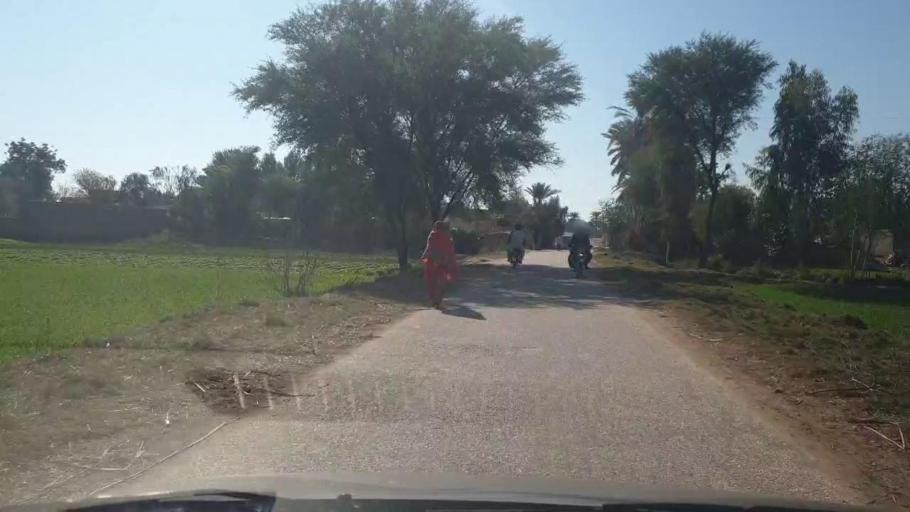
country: PK
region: Sindh
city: Bozdar
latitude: 27.1374
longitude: 68.6448
